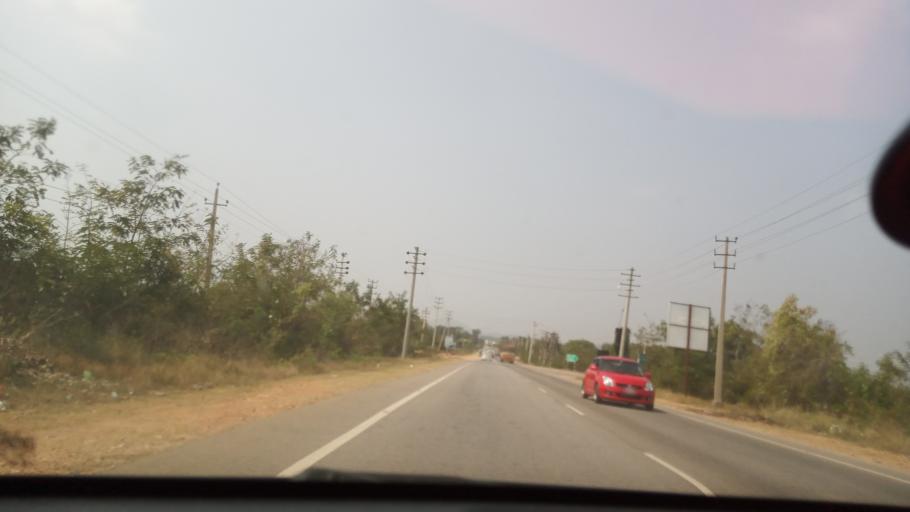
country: IN
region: Karnataka
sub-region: Chamrajnagar
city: Chamrajnagar
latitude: 11.9828
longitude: 76.8755
